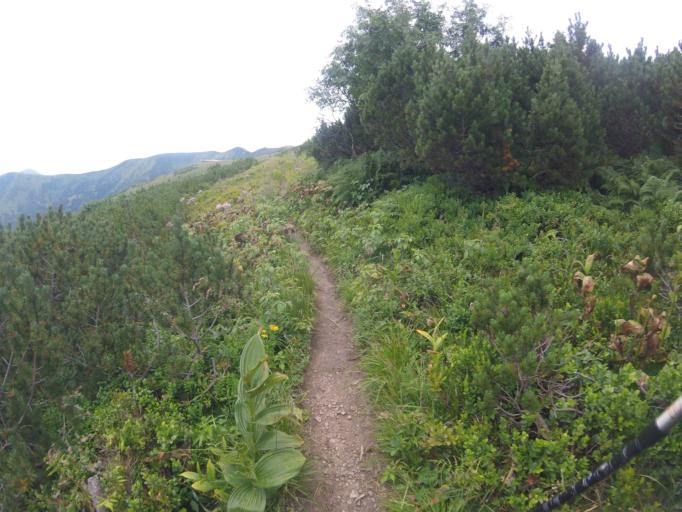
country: SK
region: Zilinsky
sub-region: Okres Zilina
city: Terchova
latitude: 49.1944
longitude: 19.0290
